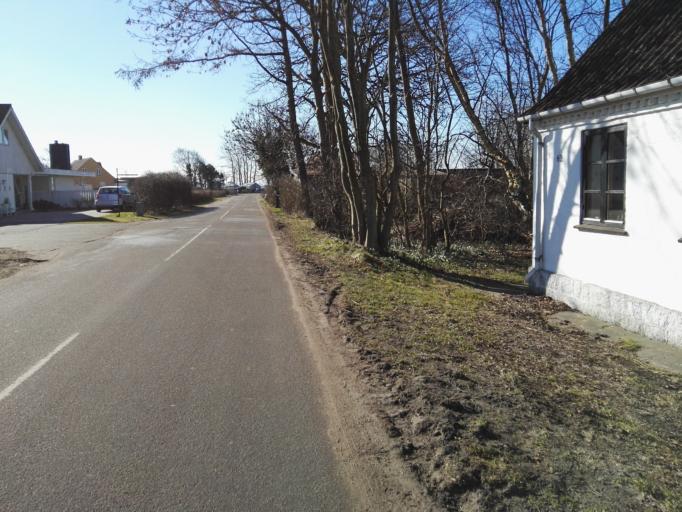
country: DK
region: Zealand
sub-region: Lejre Kommune
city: Ejby
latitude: 55.7585
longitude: 11.8030
